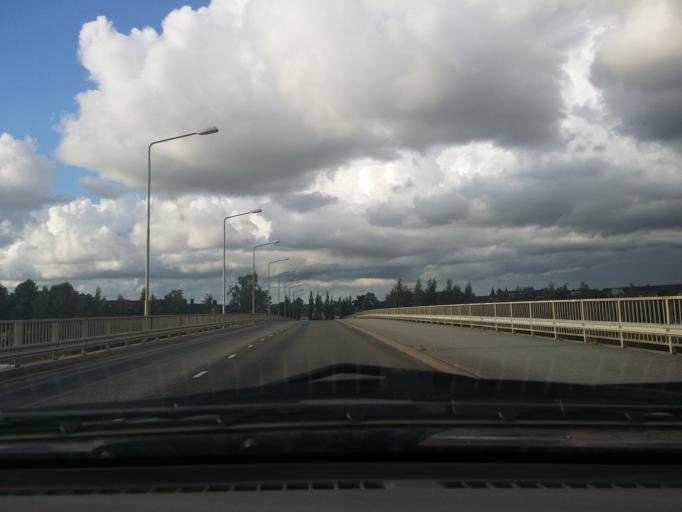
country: FI
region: Satakunta
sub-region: Pori
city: Pori
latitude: 61.4904
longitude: 21.8034
